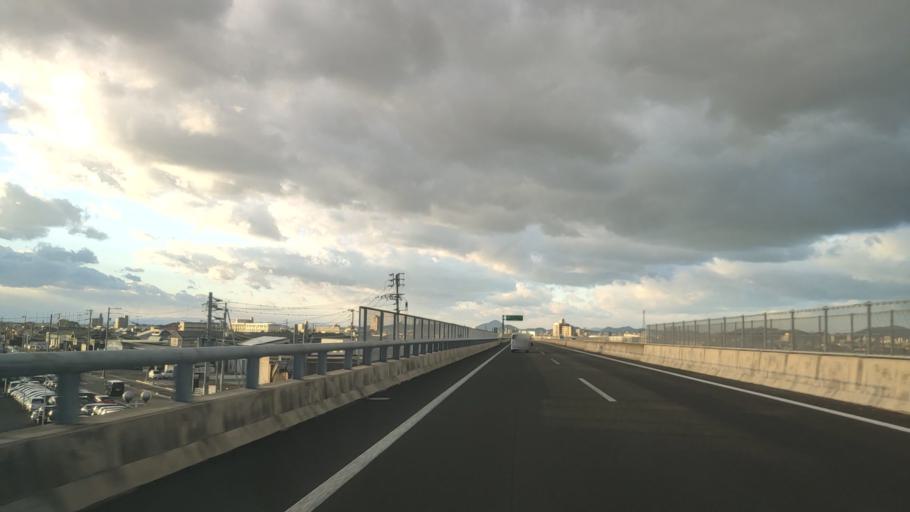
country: JP
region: Ehime
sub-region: Shikoku-chuo Shi
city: Matsuyama
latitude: 33.7908
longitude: 132.8040
